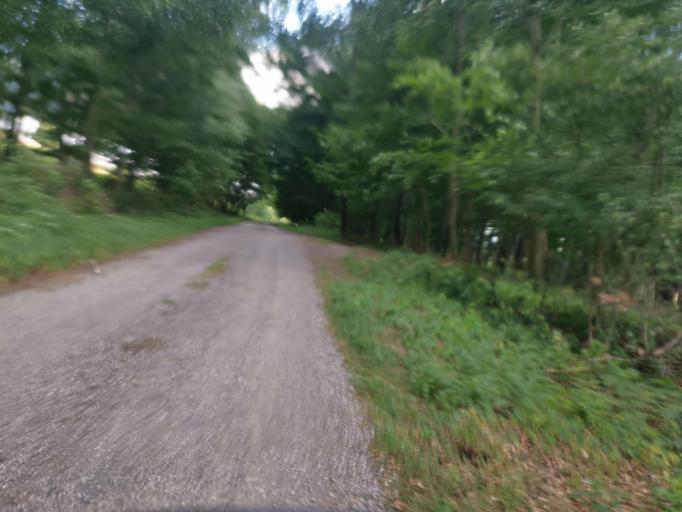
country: CZ
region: South Moravian
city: Knezdub
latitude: 48.8167
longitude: 17.4179
